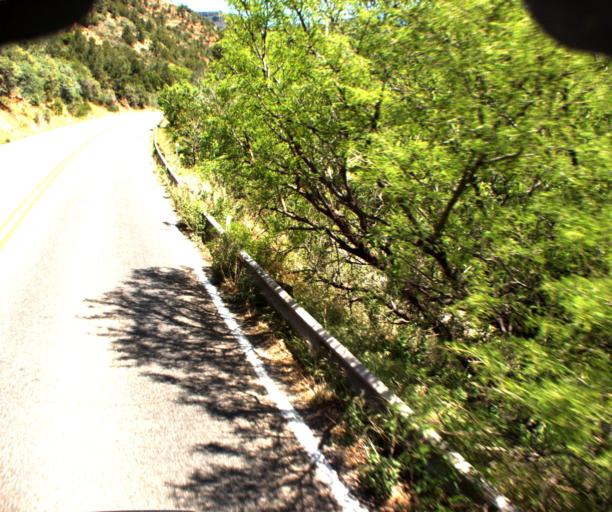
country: US
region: Arizona
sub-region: Coconino County
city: Sedona
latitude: 34.8984
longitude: -111.7318
